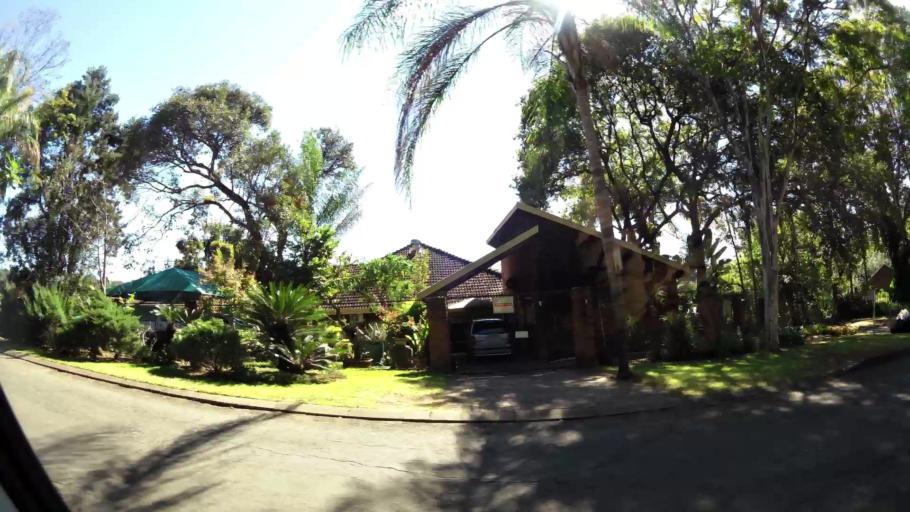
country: ZA
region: Limpopo
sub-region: Mopani District Municipality
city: Tzaneen
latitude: -23.8334
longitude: 30.1488
